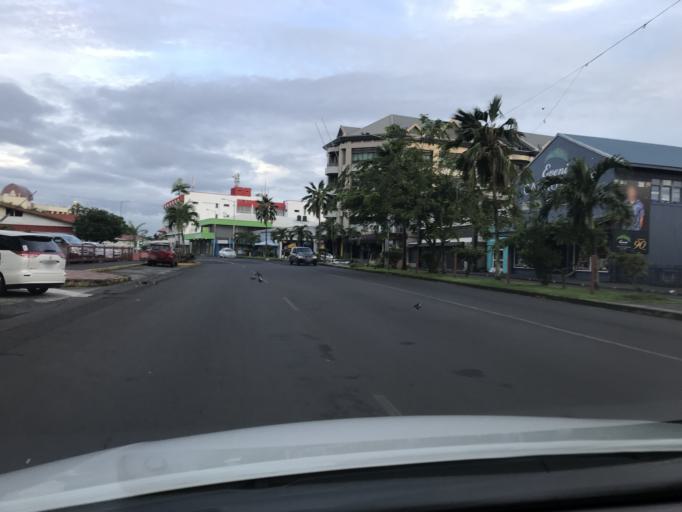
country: WS
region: Tuamasaga
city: Apia
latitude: -13.8301
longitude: -171.7705
